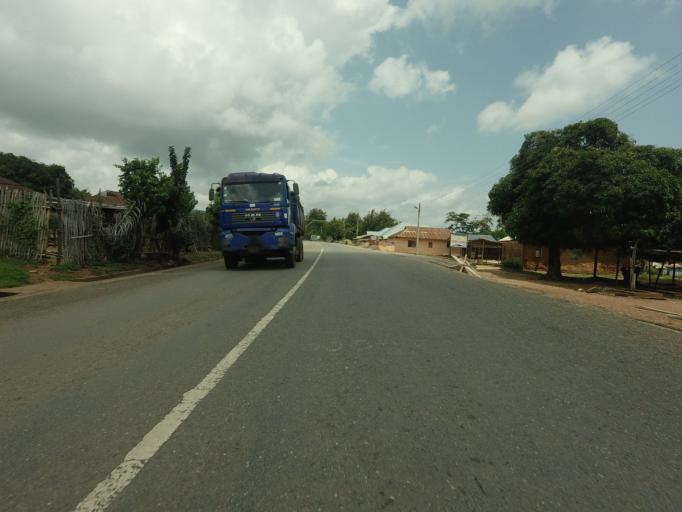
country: GH
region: Volta
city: Ho
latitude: 6.7099
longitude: 0.3350
